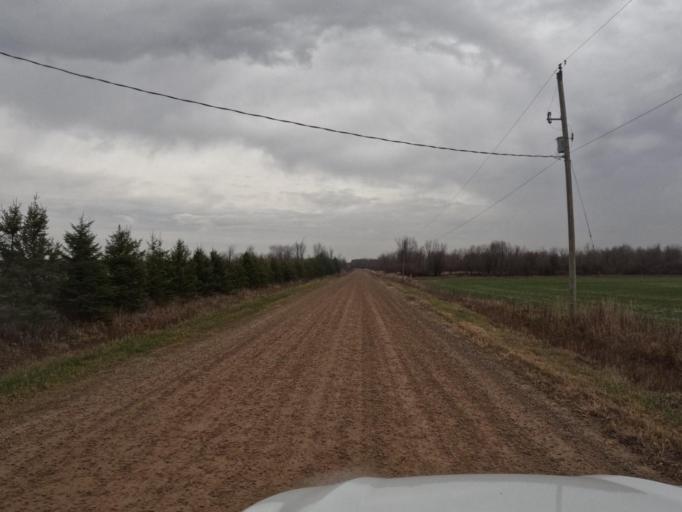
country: CA
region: Ontario
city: Shelburne
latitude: 43.8924
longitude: -80.3836
